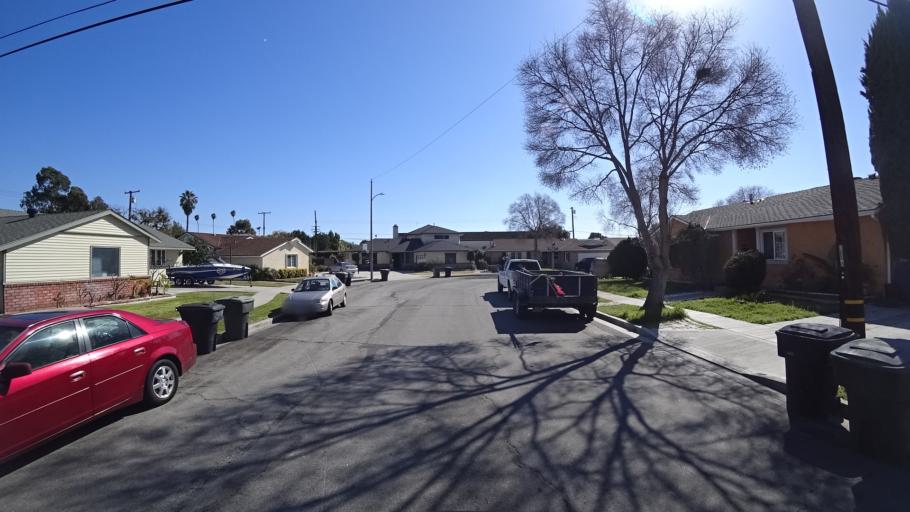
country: US
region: California
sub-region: Orange County
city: Stanton
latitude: 33.8340
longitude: -117.9617
